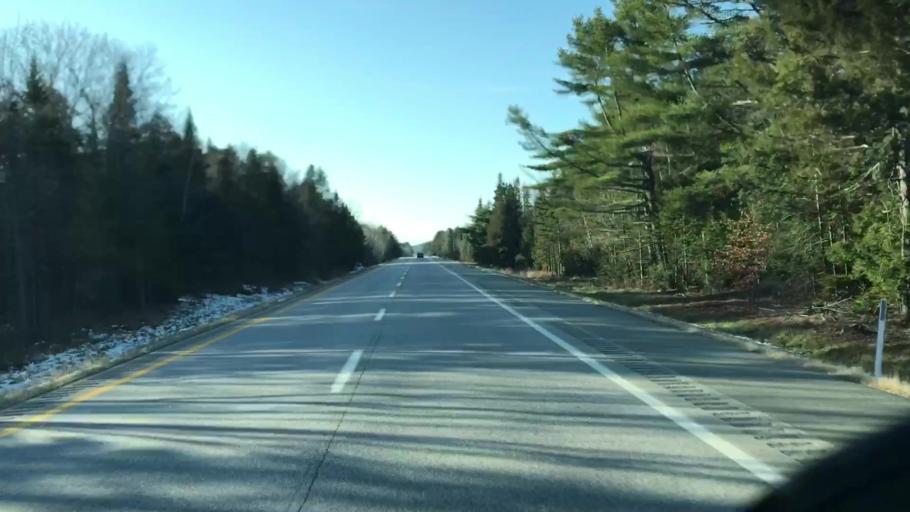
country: US
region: Maine
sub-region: Penobscot County
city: Carmel
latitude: 44.7798
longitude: -69.0691
